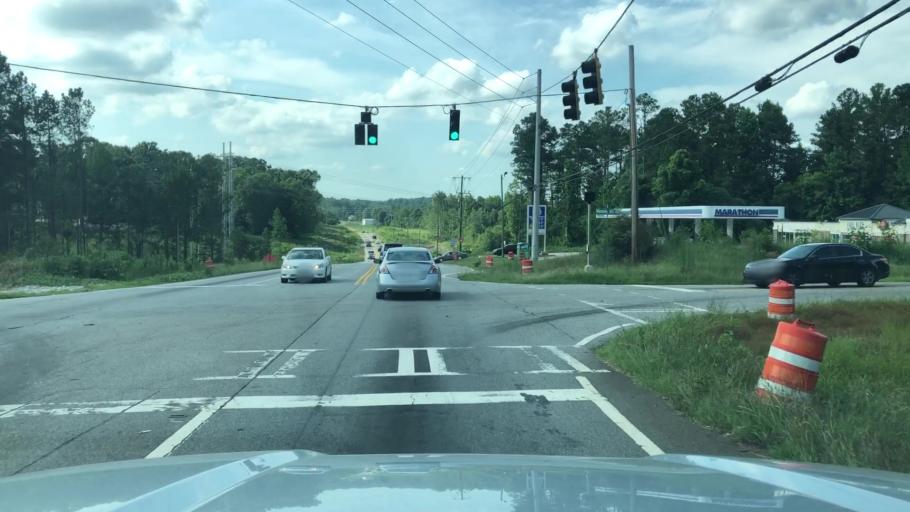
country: US
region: Georgia
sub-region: Douglas County
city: Douglasville
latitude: 33.7813
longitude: -84.7481
